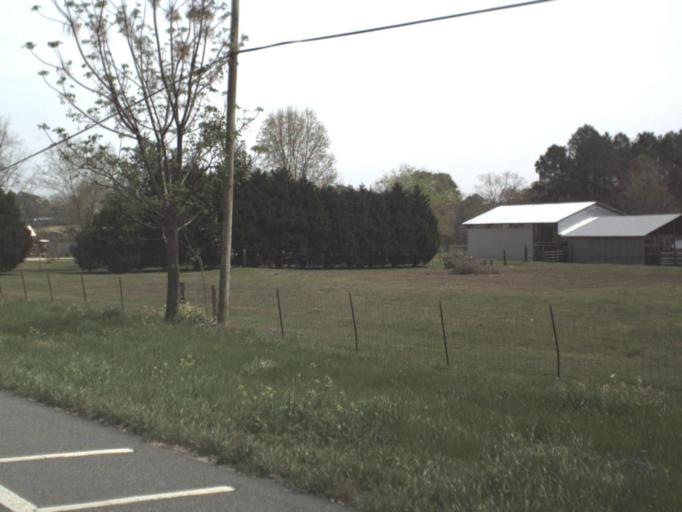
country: US
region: Florida
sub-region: Jackson County
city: Graceville
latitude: 30.9648
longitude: -85.5741
